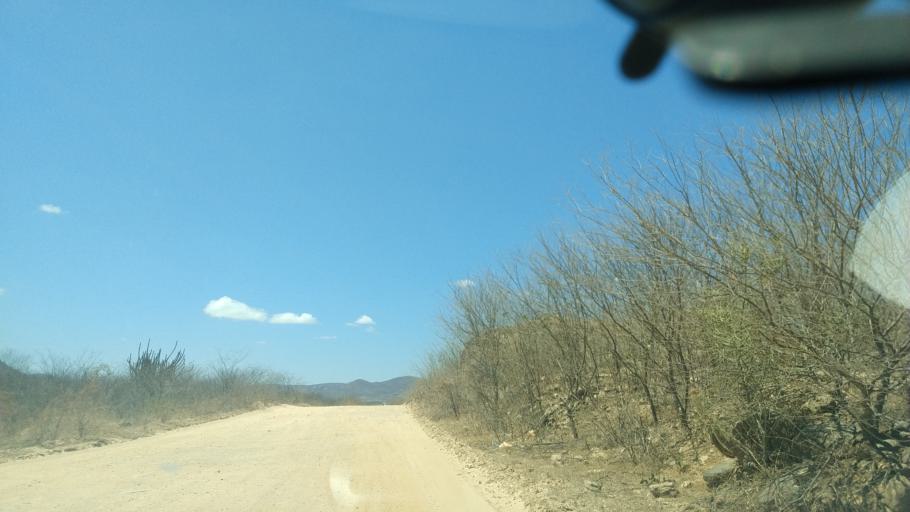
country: BR
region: Rio Grande do Norte
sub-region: Sao Tome
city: Sao Tome
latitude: -5.9723
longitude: -36.1646
